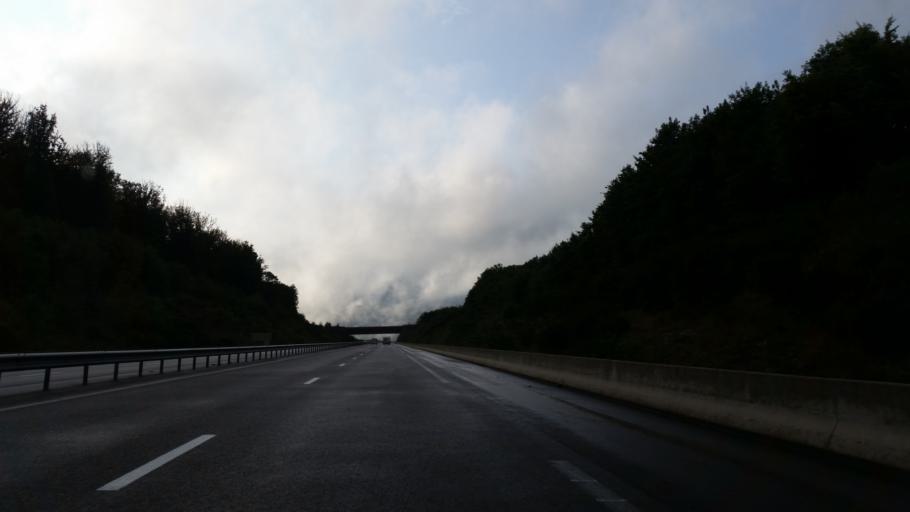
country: FR
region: Franche-Comte
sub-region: Departement de la Haute-Saone
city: Froideconche
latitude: 47.8406
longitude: 6.3991
